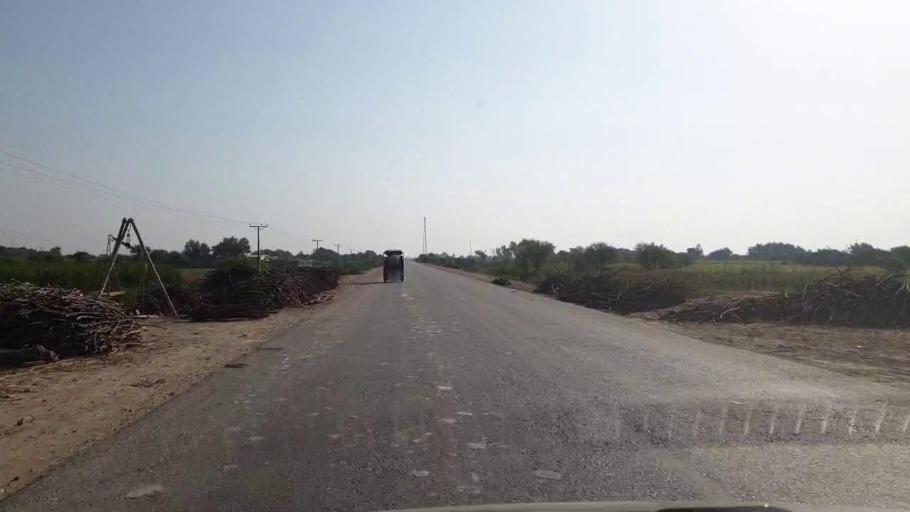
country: PK
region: Sindh
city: Badin
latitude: 24.6586
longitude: 68.9447
